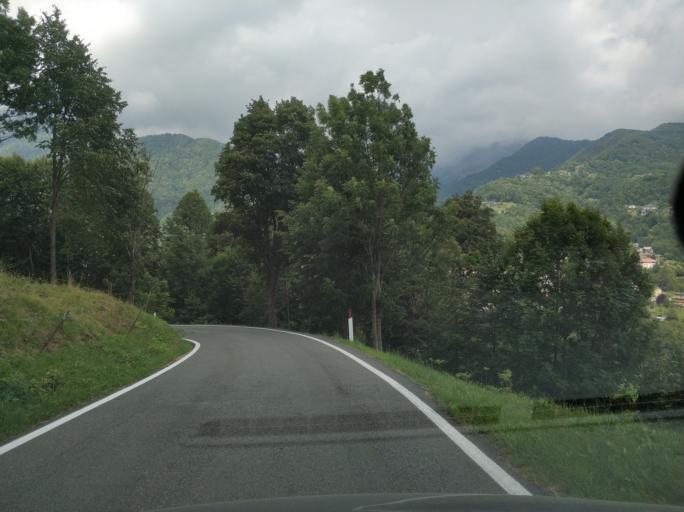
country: IT
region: Piedmont
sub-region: Provincia di Torino
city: Viu
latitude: 45.2292
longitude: 7.3747
